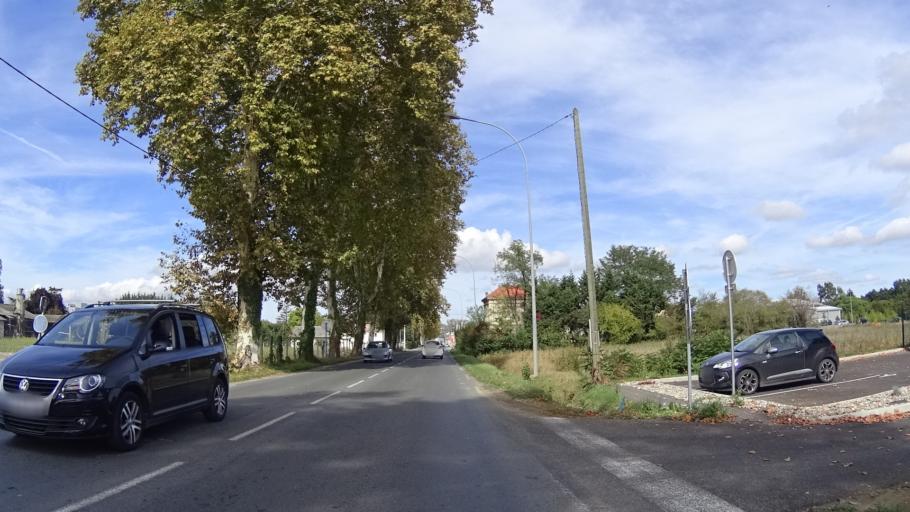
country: FR
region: Aquitaine
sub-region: Departement du Lot-et-Garonne
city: Agen
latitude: 44.1836
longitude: 0.6327
